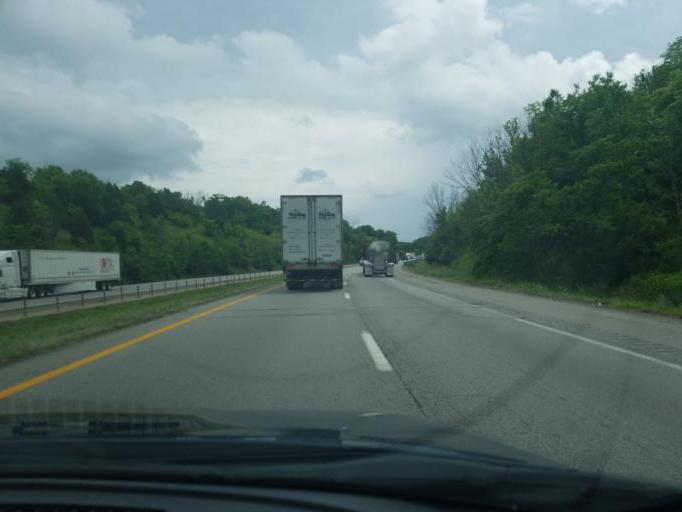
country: US
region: Kentucky
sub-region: Trimble County
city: Providence
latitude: 38.5874
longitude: -85.1755
